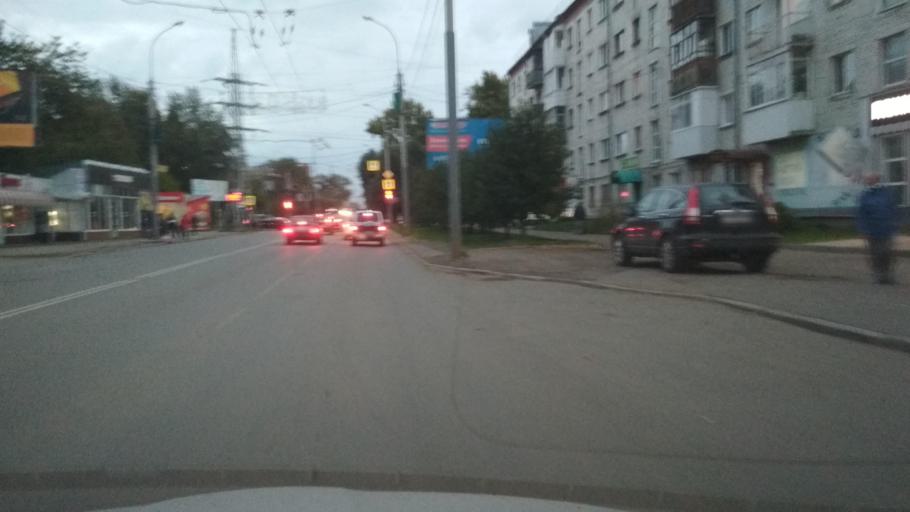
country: RU
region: Tomsk
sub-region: Tomskiy Rayon
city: Tomsk
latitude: 56.4761
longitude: 84.9902
